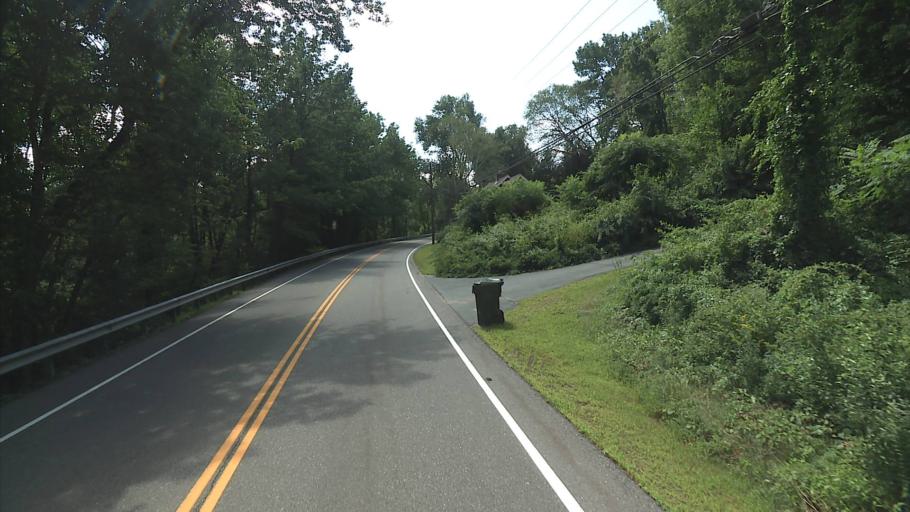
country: US
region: Connecticut
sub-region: Windham County
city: South Woodstock
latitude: 41.9521
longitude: -72.0757
